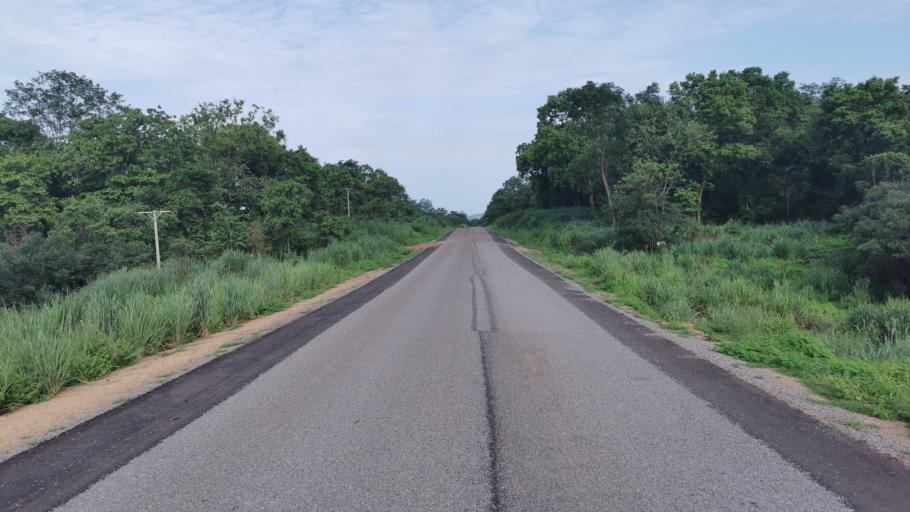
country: ET
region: Gambela
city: Gambela
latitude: 7.8193
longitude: 34.6228
